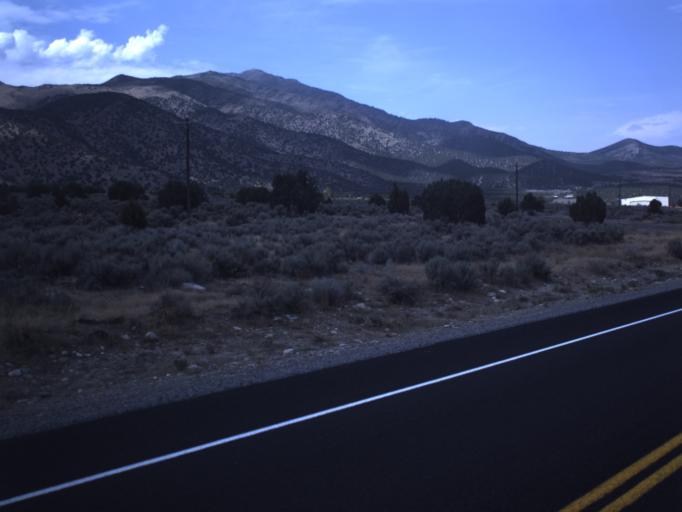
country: US
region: Utah
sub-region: Utah County
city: Eagle Mountain
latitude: 40.3171
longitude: -112.1025
